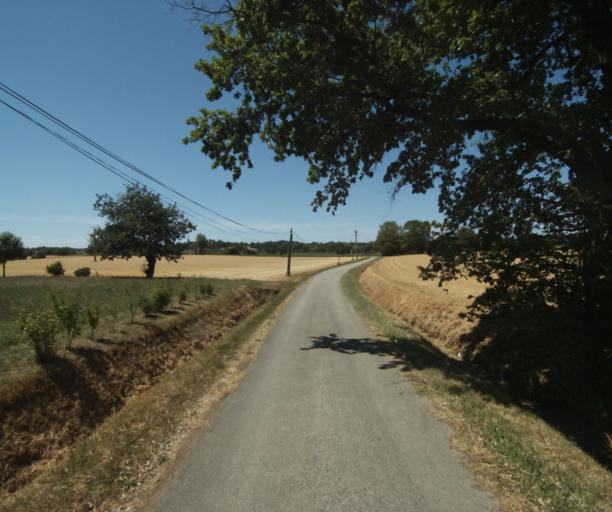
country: FR
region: Midi-Pyrenees
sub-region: Departement de la Haute-Garonne
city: Saint-Felix-Lauragais
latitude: 43.4791
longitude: 1.9383
